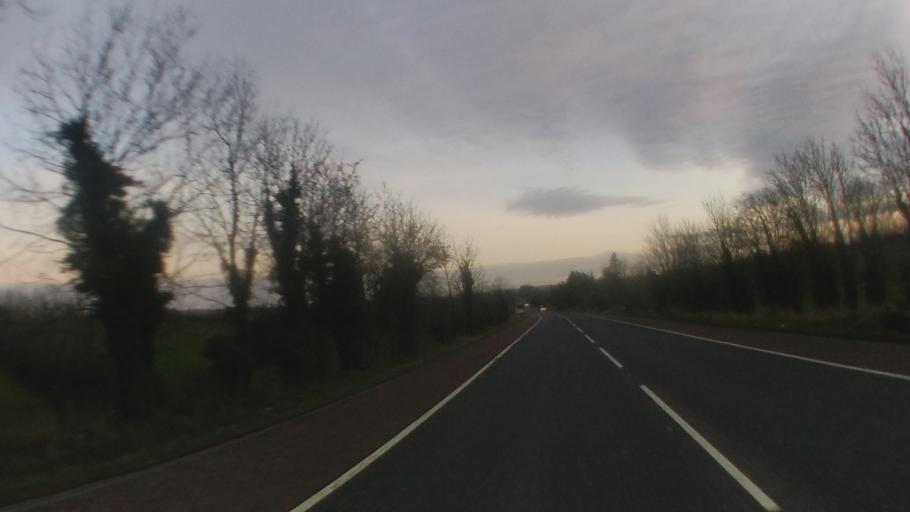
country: GB
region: Northern Ireland
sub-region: Armagh District
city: Tandragee
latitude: 54.2908
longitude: -6.5033
